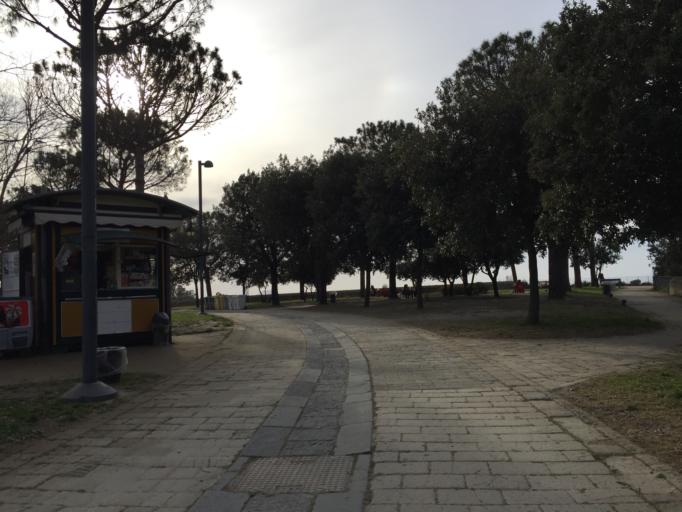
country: IT
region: Campania
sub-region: Provincia di Napoli
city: Bagnoli
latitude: 40.7995
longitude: 14.1783
